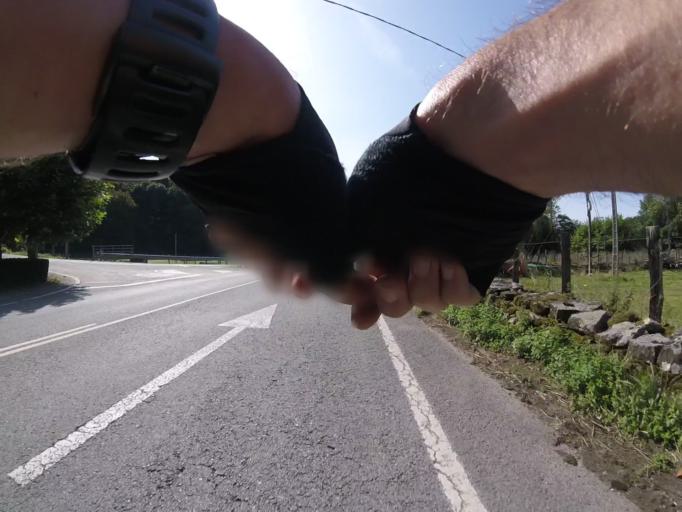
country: ES
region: Navarre
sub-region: Provincia de Navarra
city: Zugarramurdi
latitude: 43.1692
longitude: -1.4925
